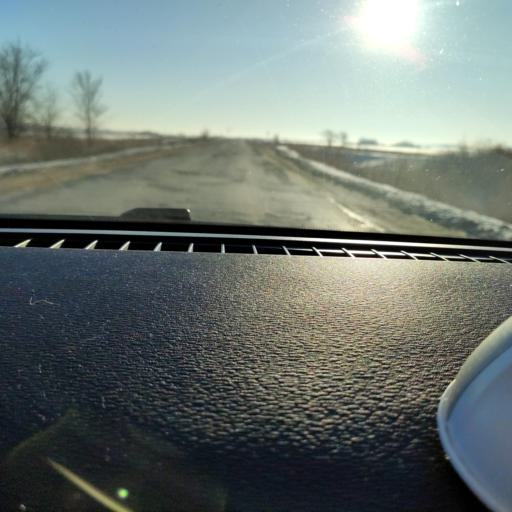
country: RU
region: Samara
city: Spiridonovka
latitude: 53.1286
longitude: 50.6165
